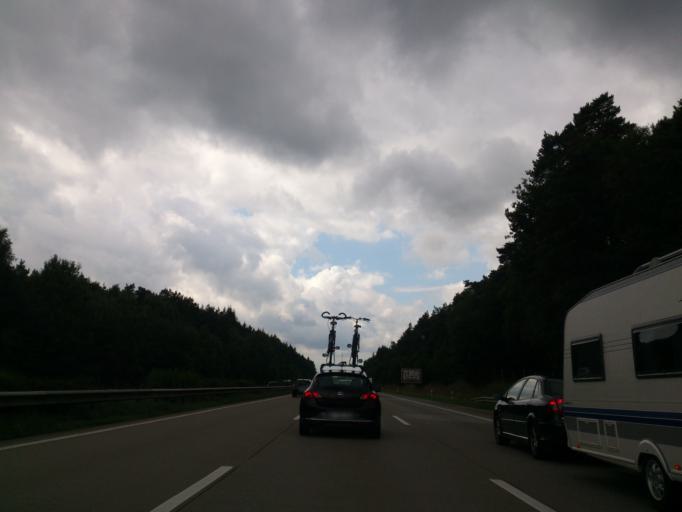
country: DE
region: Lower Saxony
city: Bispingen
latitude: 53.0288
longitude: 9.9427
